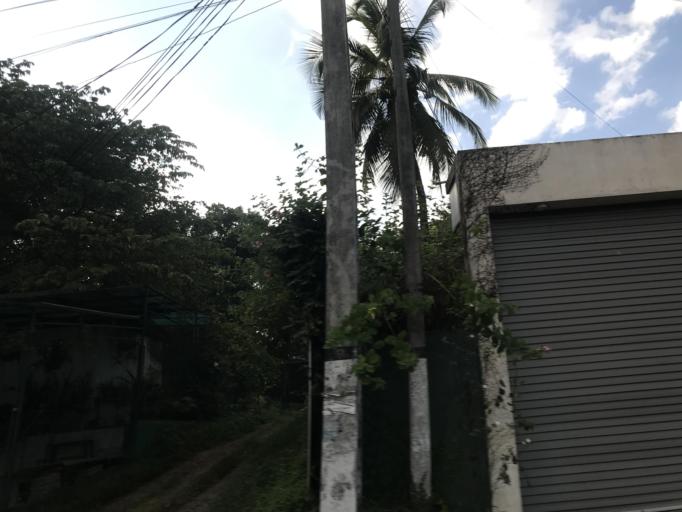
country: LK
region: Western
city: Gampaha
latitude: 7.0607
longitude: 80.0099
